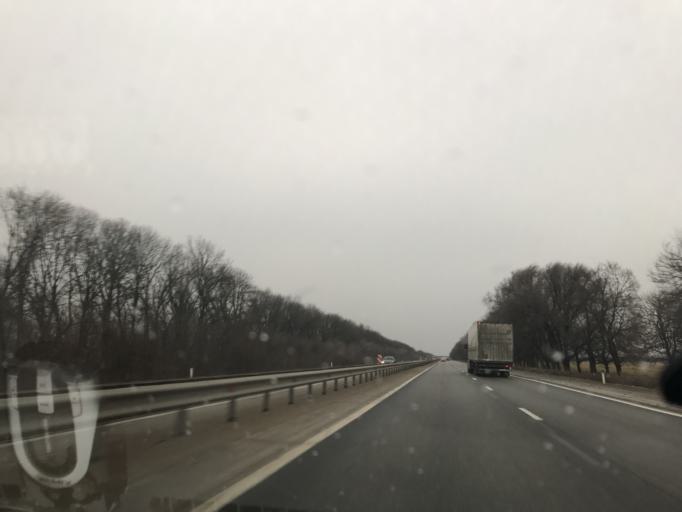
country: RU
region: Krasnodarskiy
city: Pavlovskaya
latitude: 46.1935
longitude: 39.8316
